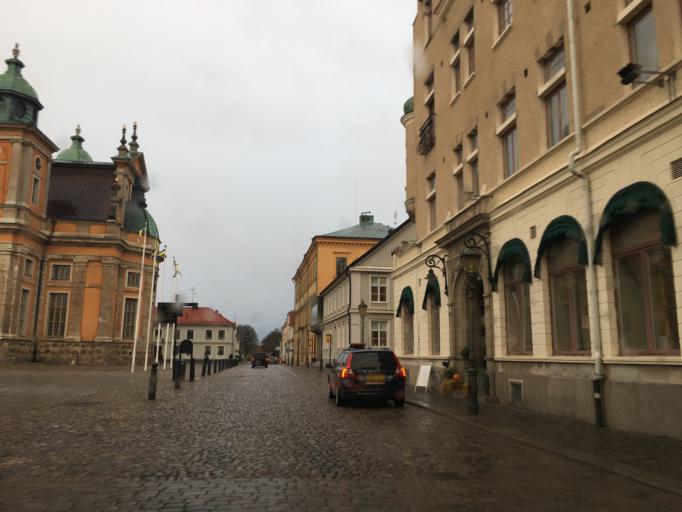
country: SE
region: Kalmar
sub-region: Kalmar Kommun
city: Kalmar
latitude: 56.6640
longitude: 16.3666
